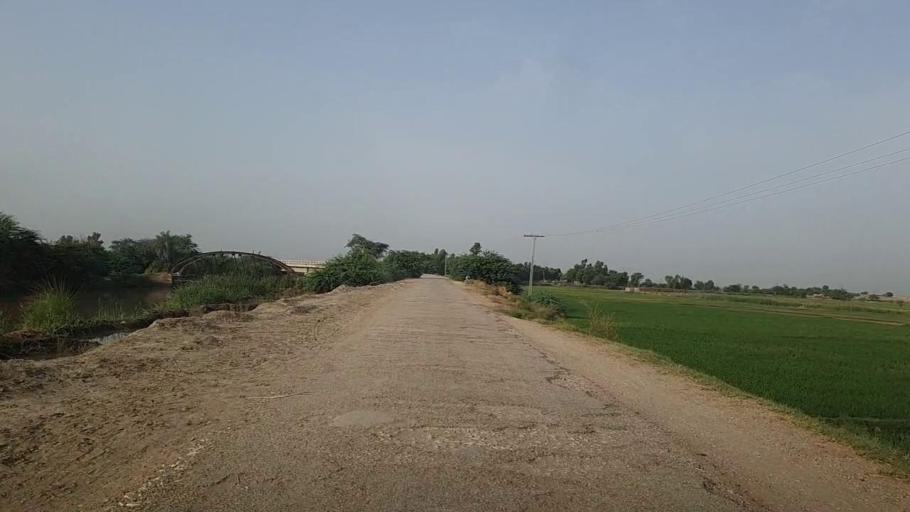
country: PK
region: Sindh
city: Mehar
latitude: 27.1295
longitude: 67.7898
